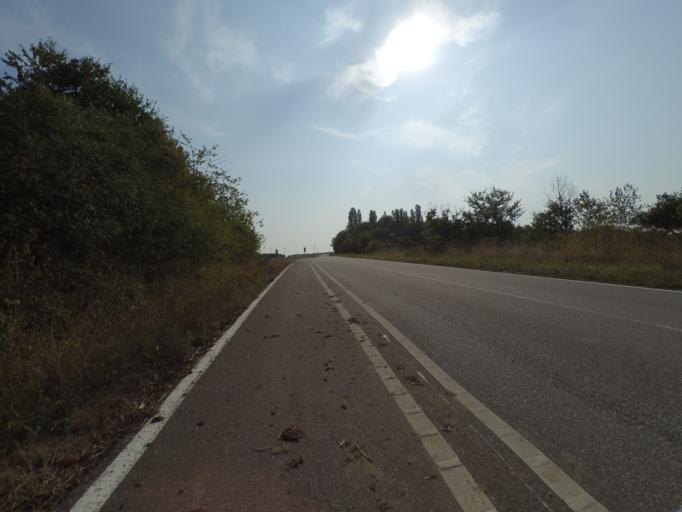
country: LU
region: Grevenmacher
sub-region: Canton de Remich
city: Remich
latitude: 49.5207
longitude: 6.3845
